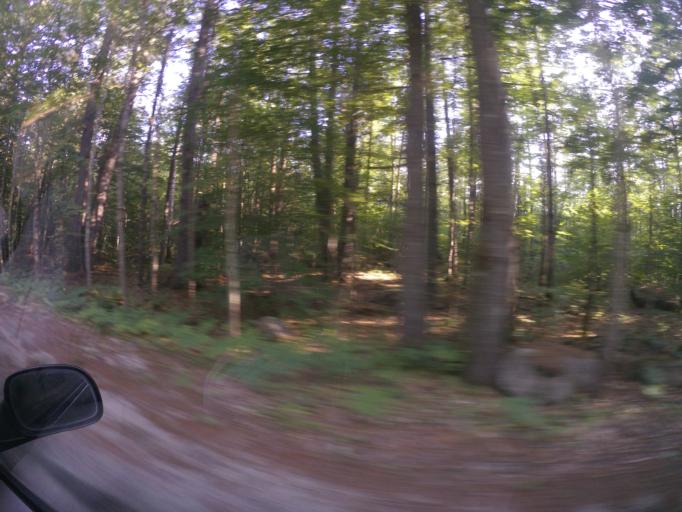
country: US
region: Maine
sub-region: Cumberland County
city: Raymond
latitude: 43.8904
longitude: -70.4375
